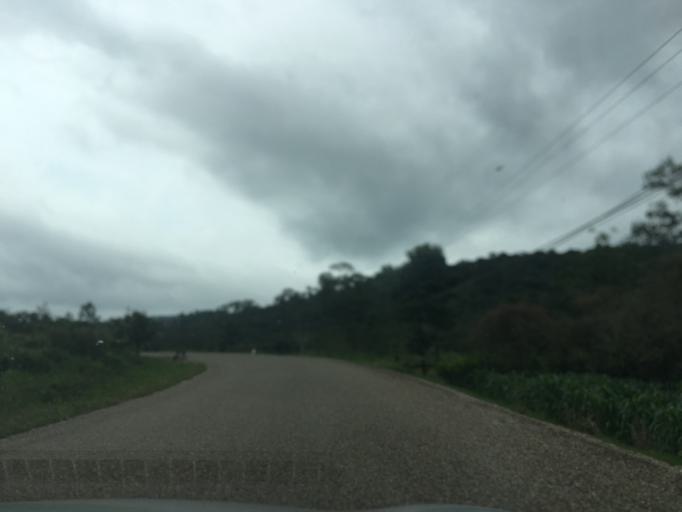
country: BZ
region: Stann Creek
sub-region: Dangriga
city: Dangriga
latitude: 17.0469
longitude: -88.5324
